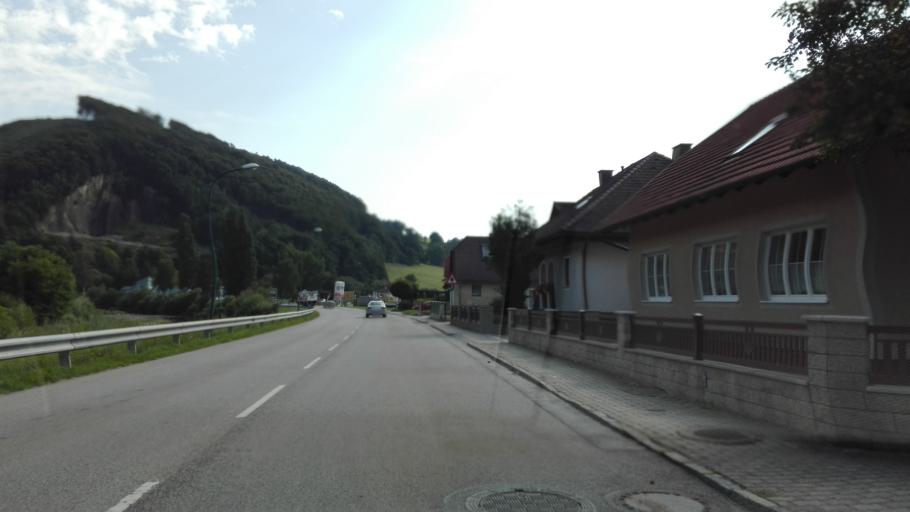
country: AT
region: Lower Austria
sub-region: Politischer Bezirk Sankt Polten
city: Rabenstein an der Pielach
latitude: 48.0678
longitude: 15.4773
